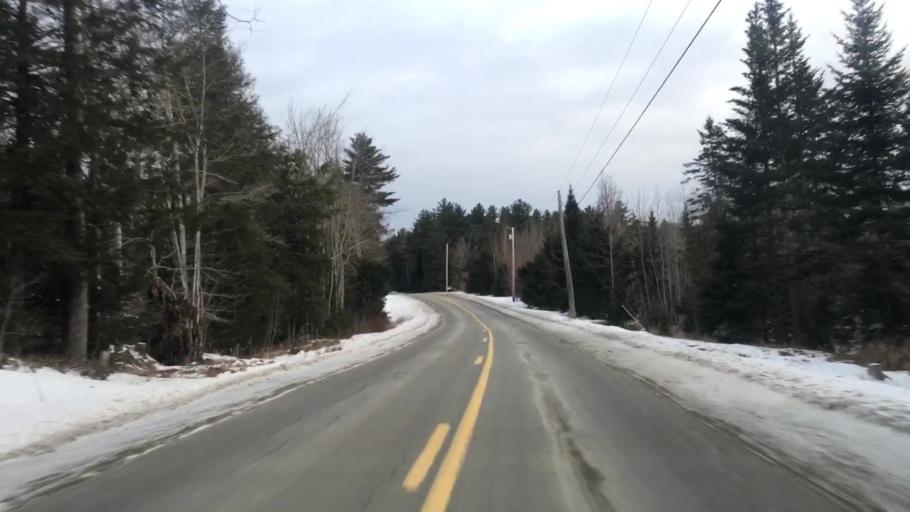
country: US
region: Maine
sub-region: Hancock County
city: Franklin
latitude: 44.7620
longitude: -68.3249
